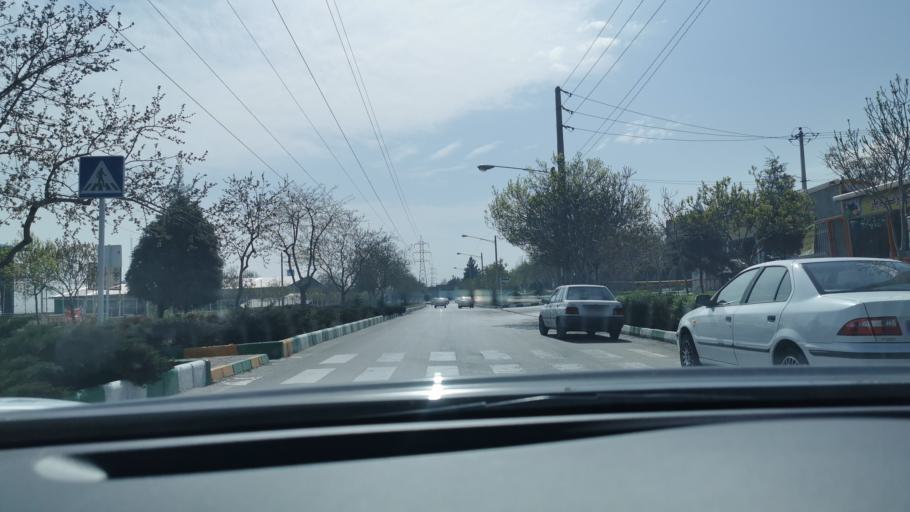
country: IR
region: Razavi Khorasan
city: Mashhad
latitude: 36.2814
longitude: 59.5472
